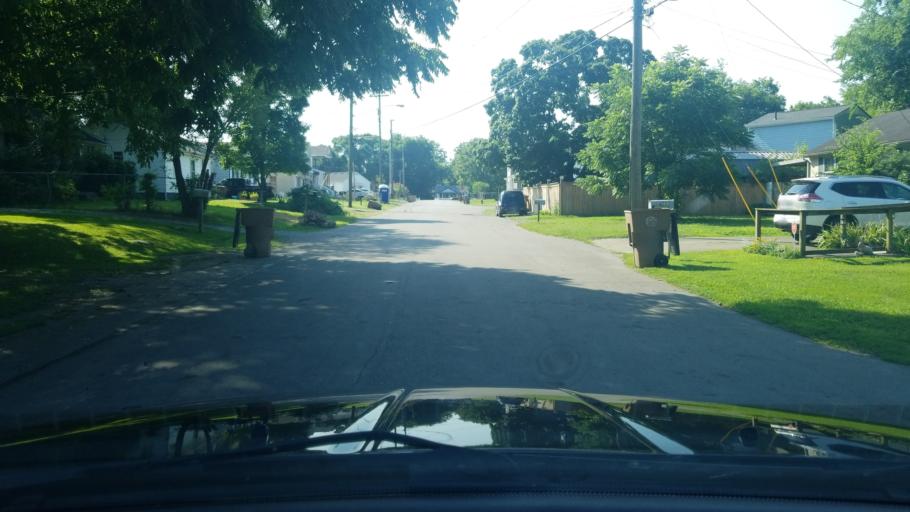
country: US
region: Tennessee
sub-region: Davidson County
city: Belle Meade
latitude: 36.1600
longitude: -86.8592
